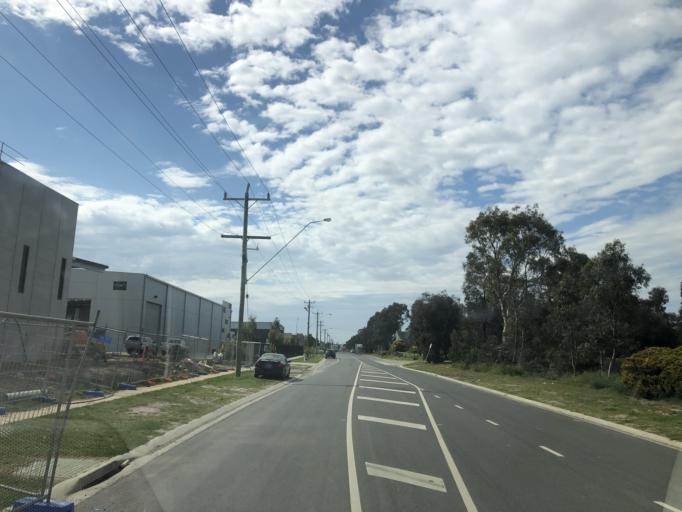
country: AU
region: Victoria
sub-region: Casey
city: Hampton Park
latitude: -38.0409
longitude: 145.2276
